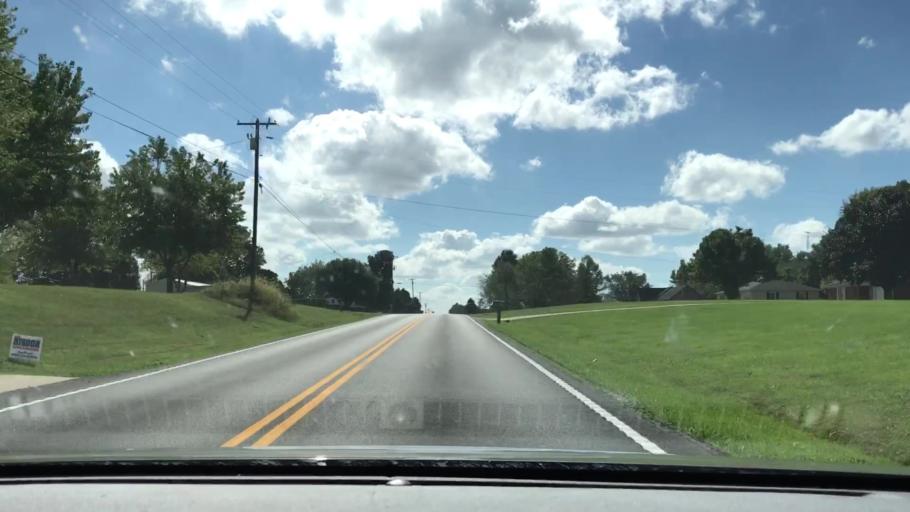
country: US
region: Kentucky
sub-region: Graves County
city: Mayfield
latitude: 36.8045
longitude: -88.5954
